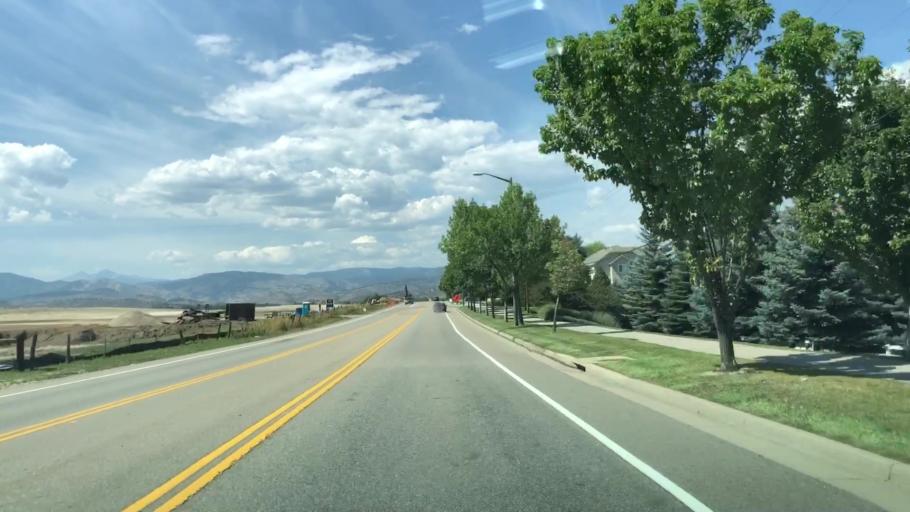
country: US
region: Colorado
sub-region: Larimer County
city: Loveland
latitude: 40.3930
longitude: -105.1344
